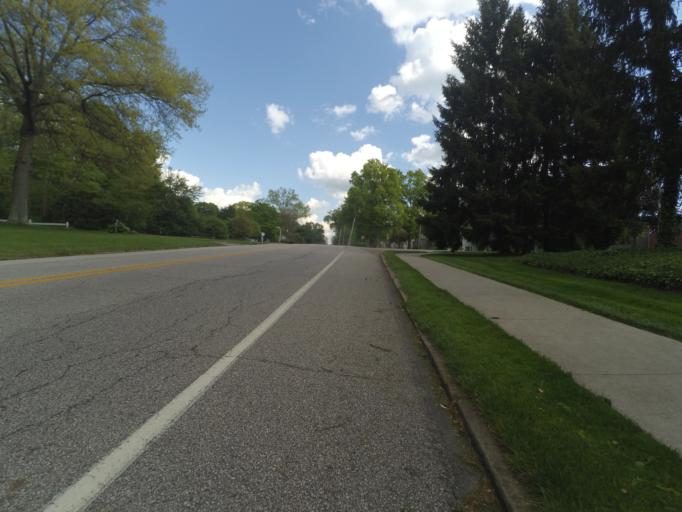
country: US
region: Ohio
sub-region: Mahoning County
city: Boardman
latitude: 41.0518
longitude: -80.6698
